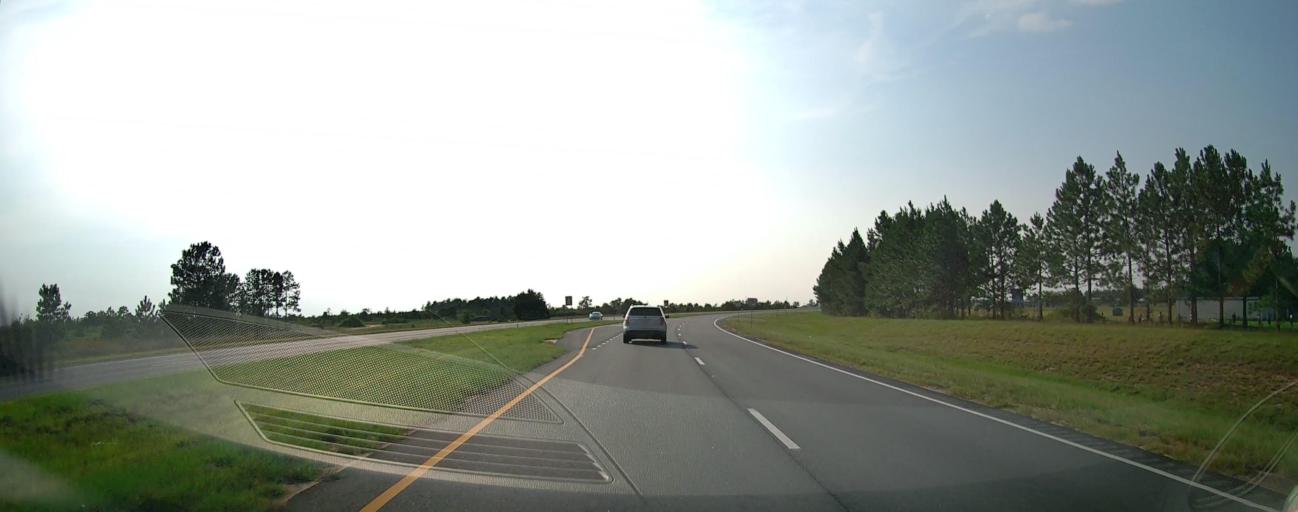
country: US
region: Georgia
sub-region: Taylor County
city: Butler
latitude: 32.5499
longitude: -84.2594
